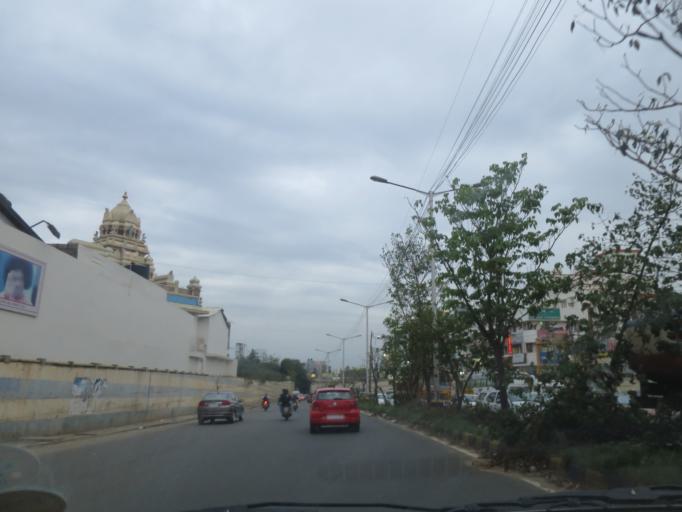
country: IN
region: Karnataka
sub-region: Bangalore Urban
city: Bangalore
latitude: 12.9593
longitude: 77.7013
